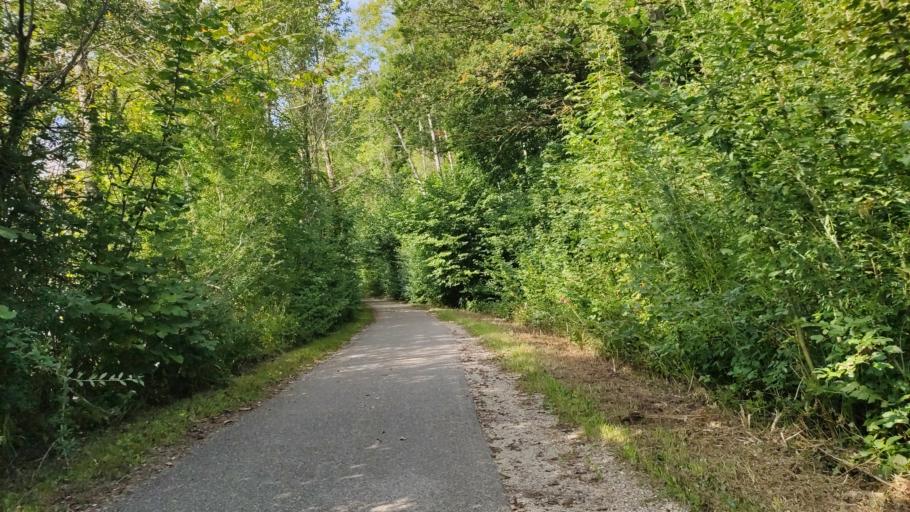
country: DE
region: Bavaria
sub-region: Upper Bavaria
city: Kaufering
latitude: 48.1110
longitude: 10.8680
